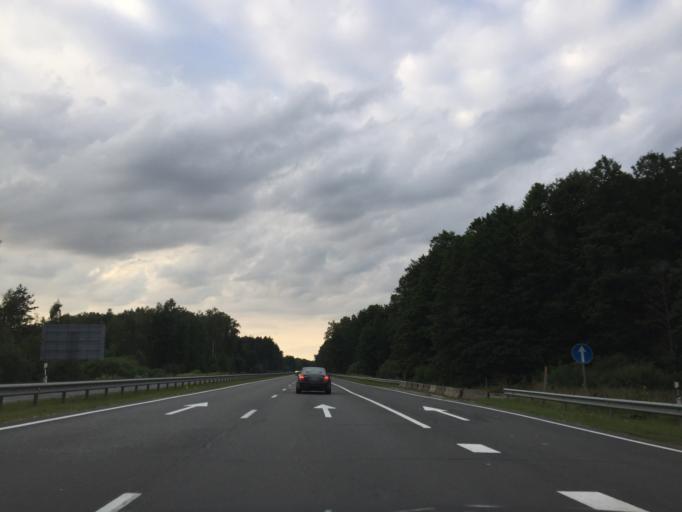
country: LV
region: Babite
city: Pinki
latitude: 56.9314
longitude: 23.9171
